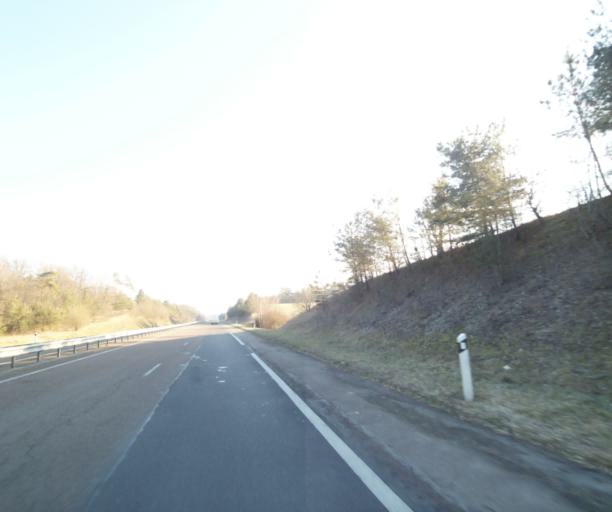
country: FR
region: Champagne-Ardenne
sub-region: Departement de la Haute-Marne
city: Chevillon
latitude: 48.5082
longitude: 5.0971
